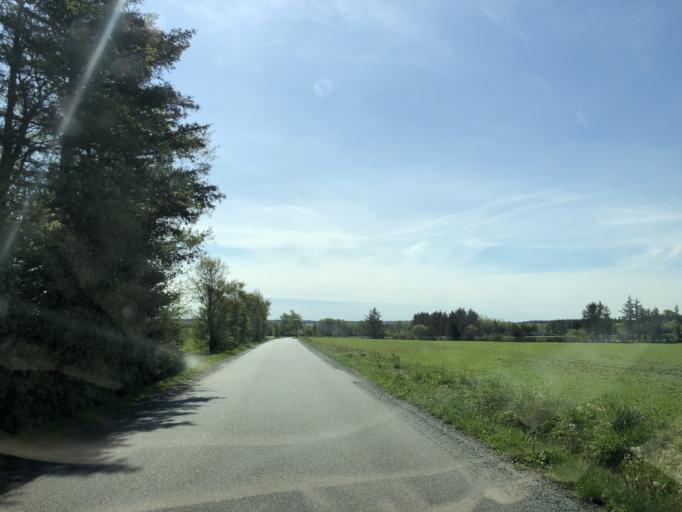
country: DK
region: Central Jutland
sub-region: Ringkobing-Skjern Kommune
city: Videbaek
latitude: 56.1680
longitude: 8.5339
